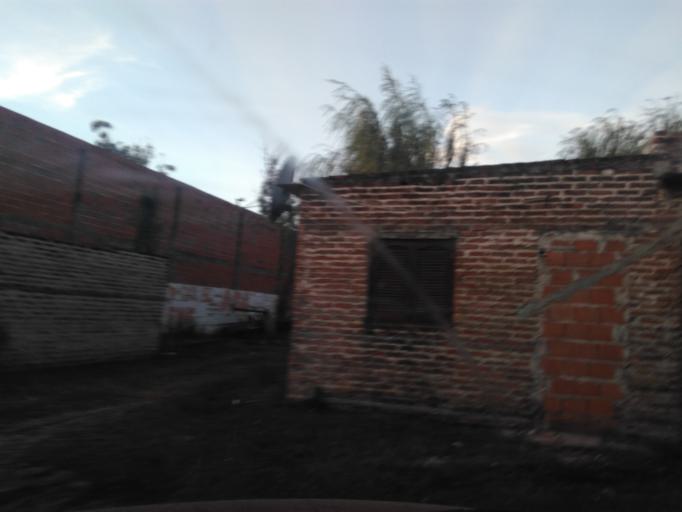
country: AR
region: Chaco
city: Fontana
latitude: -27.4566
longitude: -59.0390
